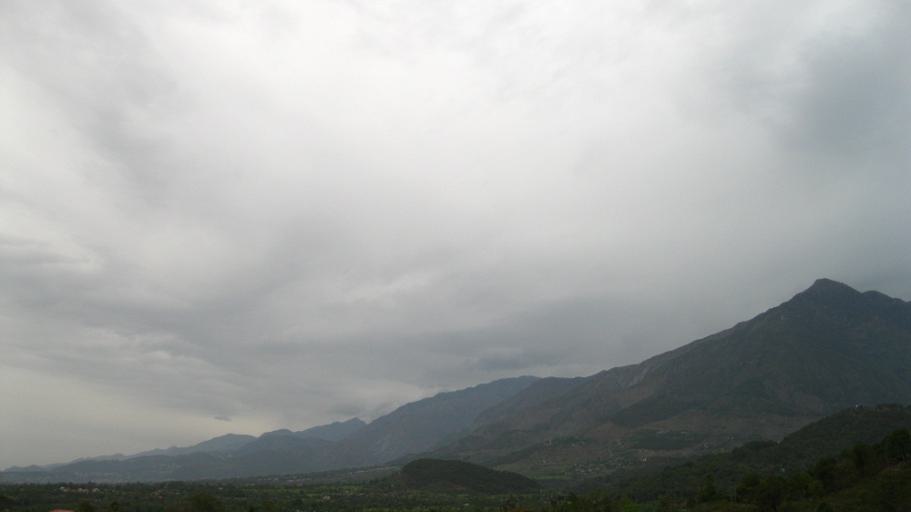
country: IN
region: Himachal Pradesh
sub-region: Kangra
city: Dharmsala
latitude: 32.1470
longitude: 76.4216
